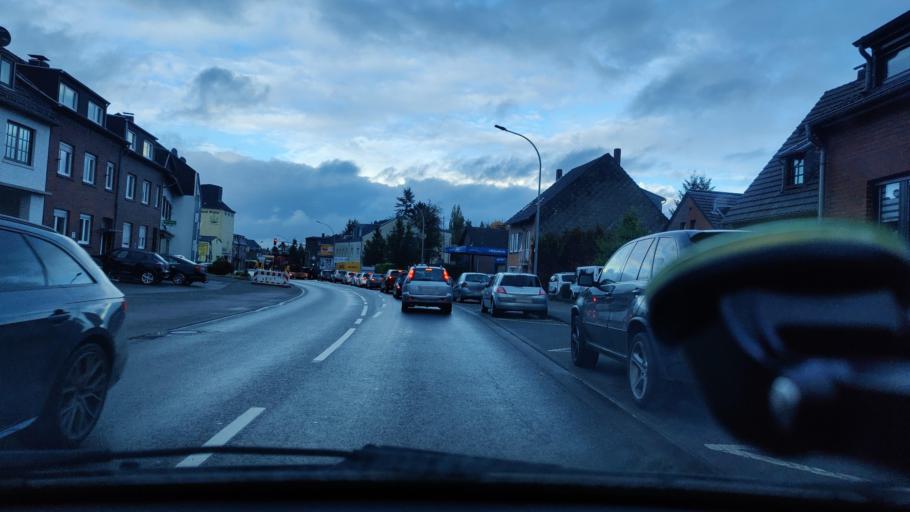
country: DE
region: North Rhine-Westphalia
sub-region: Regierungsbezirk Koln
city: Wurselen
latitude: 50.8140
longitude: 6.1528
